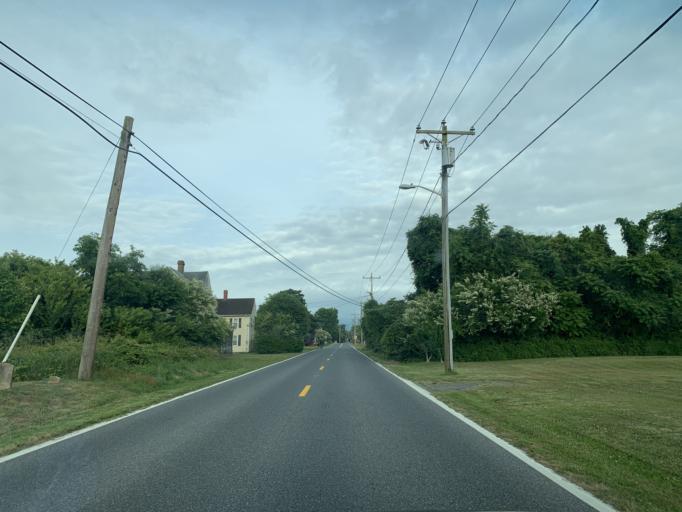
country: US
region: Virginia
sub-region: Accomack County
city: Captains Cove
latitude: 38.0560
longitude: -75.4152
